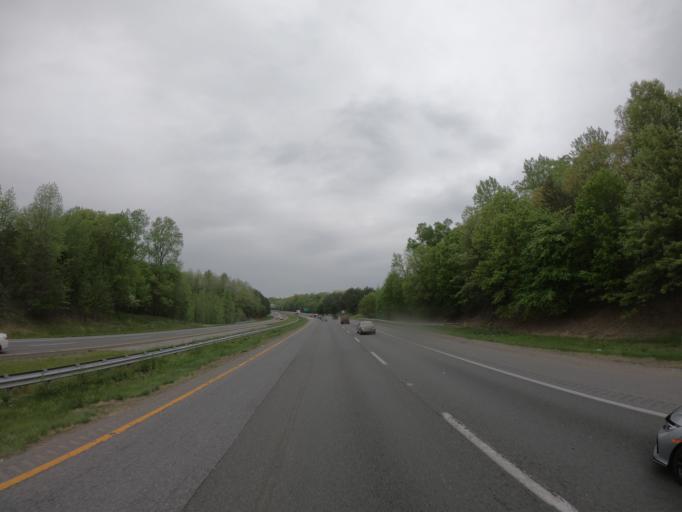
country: US
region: Maryland
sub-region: Anne Arundel County
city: Riva
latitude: 38.9907
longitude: -76.5793
